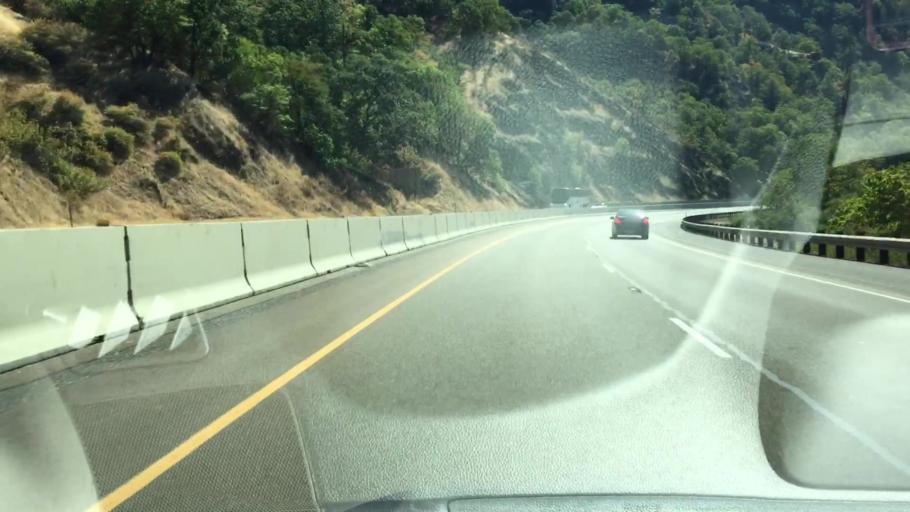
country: US
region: Oregon
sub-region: Douglas County
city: Tri-City
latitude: 42.9624
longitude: -123.3278
